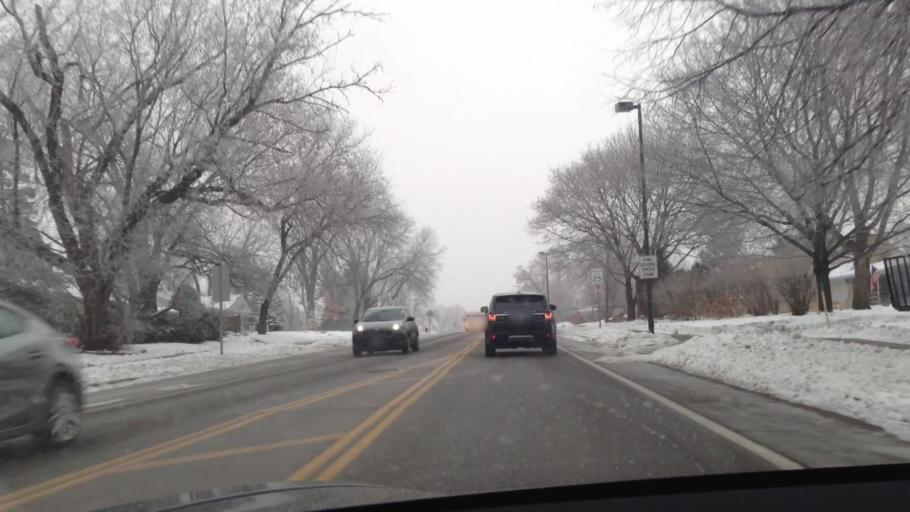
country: US
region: Minnesota
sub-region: Hennepin County
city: Edina
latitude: 44.8764
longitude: -93.3353
